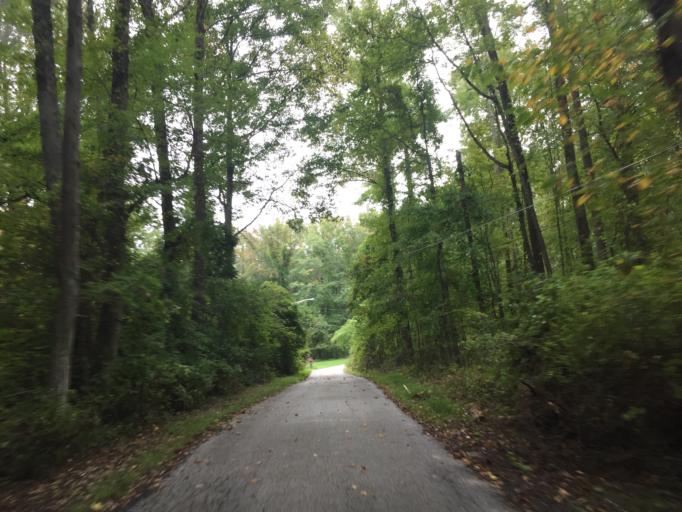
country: US
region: Maryland
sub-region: Baltimore County
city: Middle River
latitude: 39.3469
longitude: -76.4275
